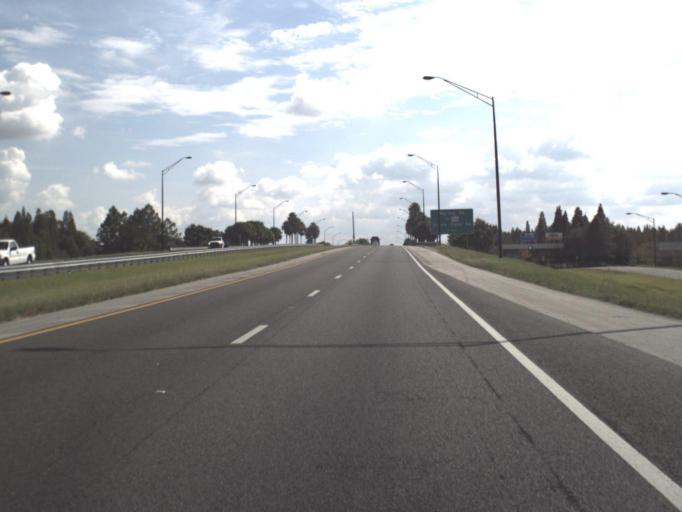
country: US
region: Florida
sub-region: Polk County
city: Winston
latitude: 28.0093
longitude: -82.0198
